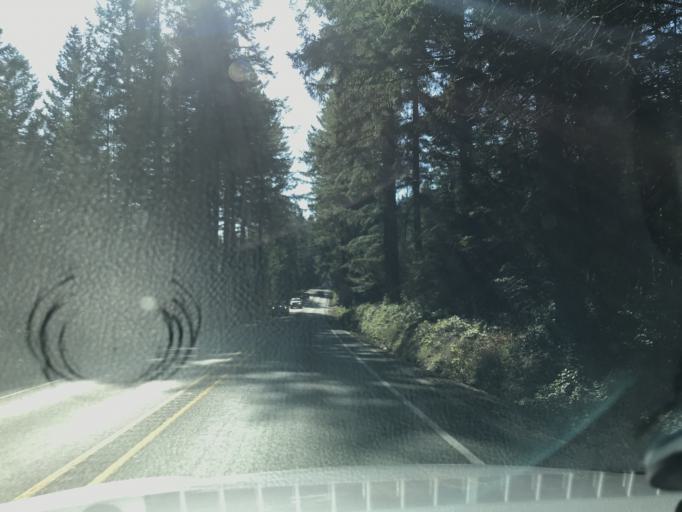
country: US
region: Washington
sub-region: Pierce County
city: Key Center
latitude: 47.3654
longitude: -122.7227
